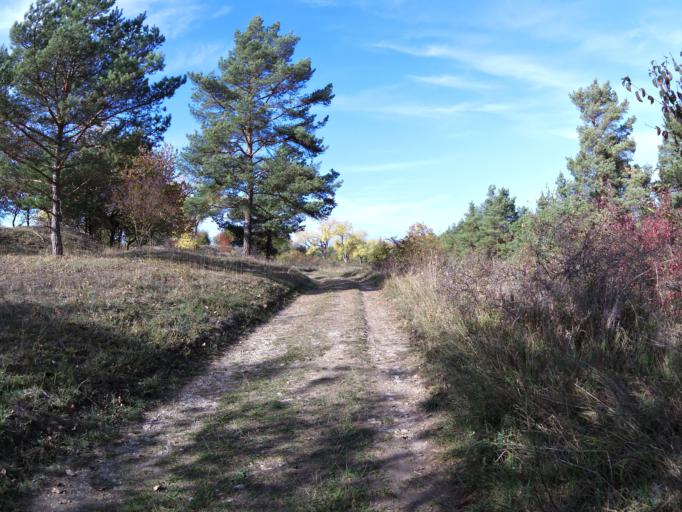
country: DE
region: Bavaria
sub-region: Regierungsbezirk Unterfranken
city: Winterhausen
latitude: 49.7062
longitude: 10.0008
